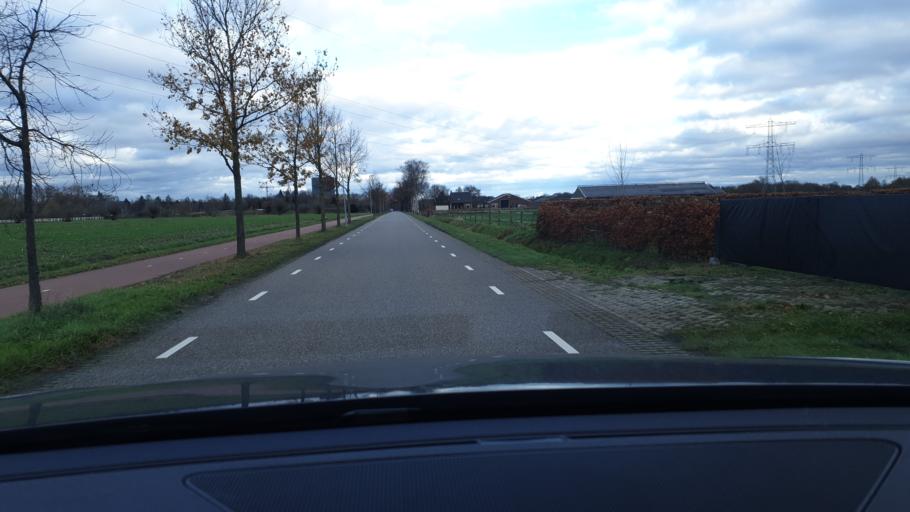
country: NL
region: North Brabant
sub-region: Gemeente Veldhoven
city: Veldhoven
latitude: 51.3903
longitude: 5.4099
